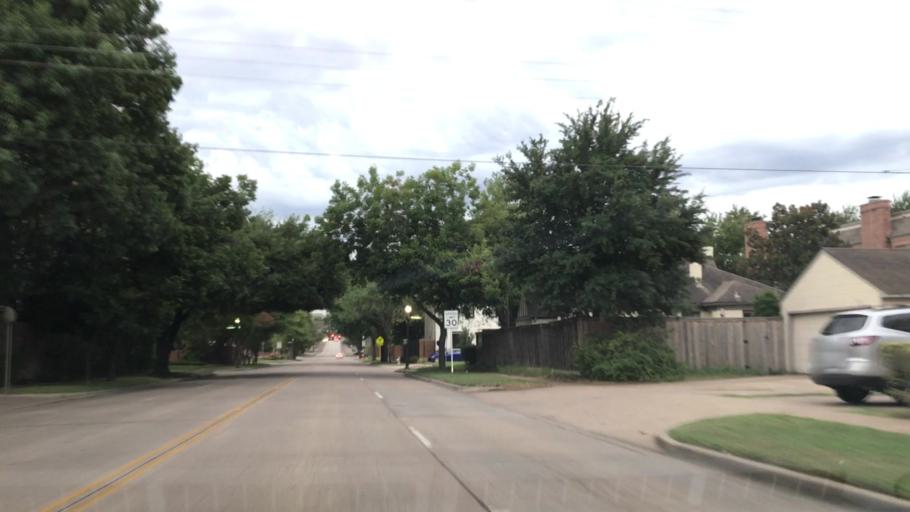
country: US
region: Texas
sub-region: Dallas County
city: University Park
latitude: 32.8537
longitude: -96.7870
